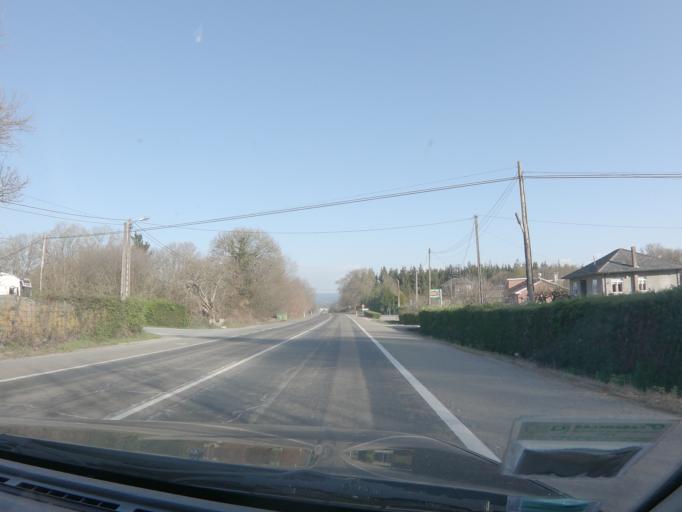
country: ES
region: Galicia
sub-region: Provincia de Lugo
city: Corgo
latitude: 42.9525
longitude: -7.4610
